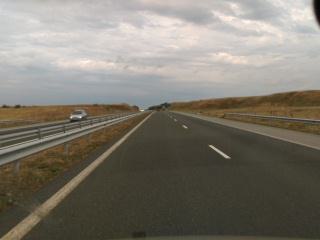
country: BG
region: Yambol
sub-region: Obshtina Yambol
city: Yambol
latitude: 42.5425
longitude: 26.4624
